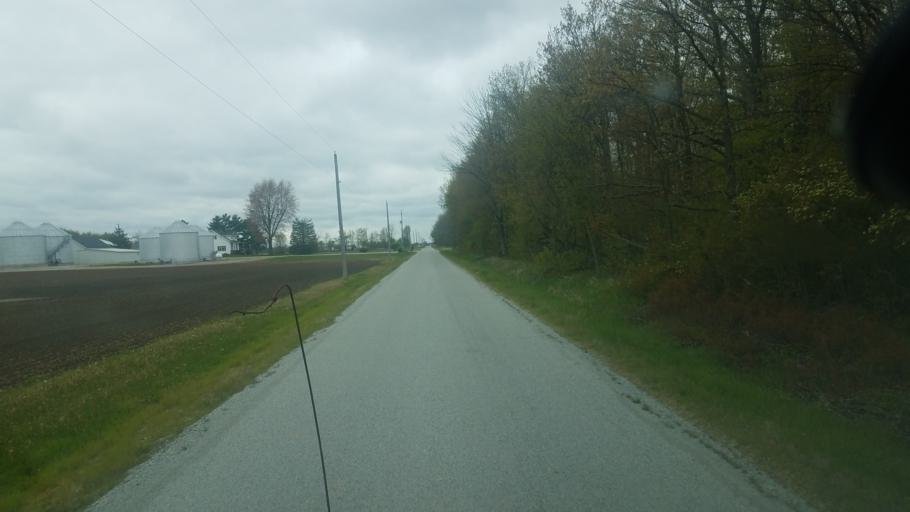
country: US
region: Ohio
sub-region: Hardin County
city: Forest
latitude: 40.7237
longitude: -83.5479
